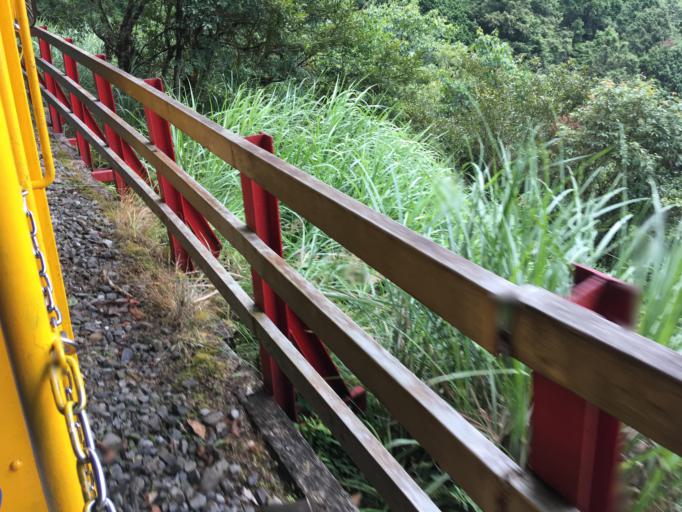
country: TW
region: Taiwan
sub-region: Yilan
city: Yilan
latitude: 24.4904
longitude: 121.5330
